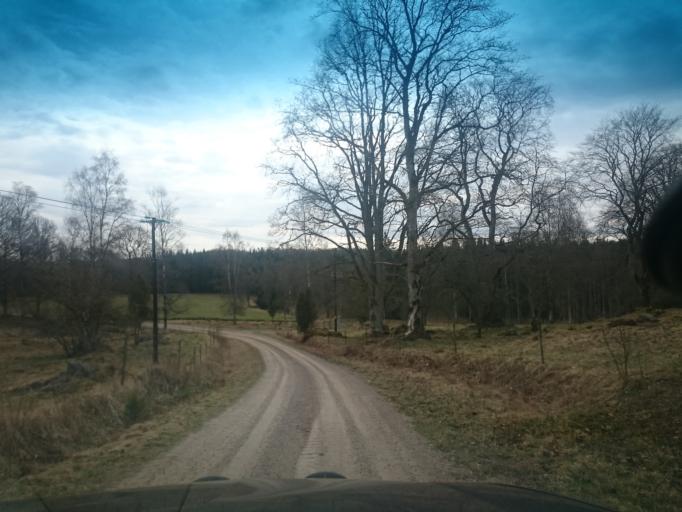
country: SE
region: Joenkoeping
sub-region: Vetlanda Kommun
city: Vetlanda
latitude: 57.3402
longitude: 15.1477
